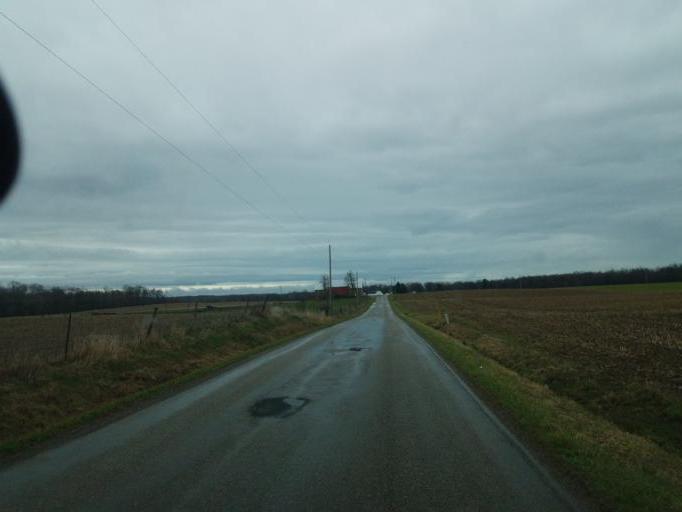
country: US
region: Ohio
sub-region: Richland County
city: Lexington
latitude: 40.6628
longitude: -82.6678
